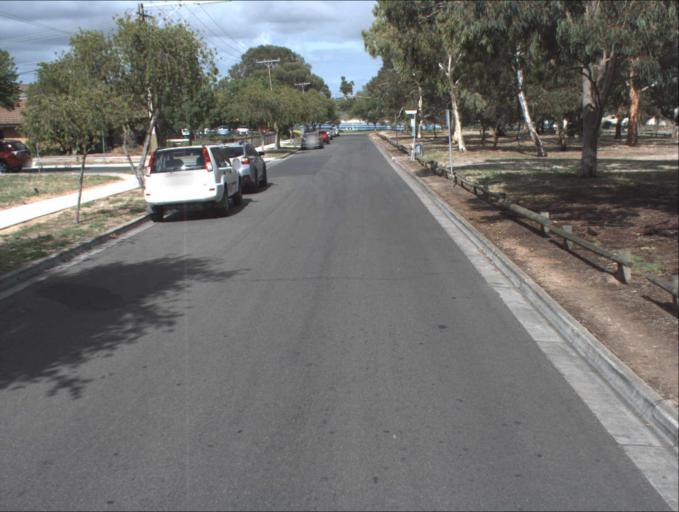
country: AU
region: South Australia
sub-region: Port Adelaide Enfield
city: Gilles Plains
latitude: -34.8526
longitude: 138.6623
